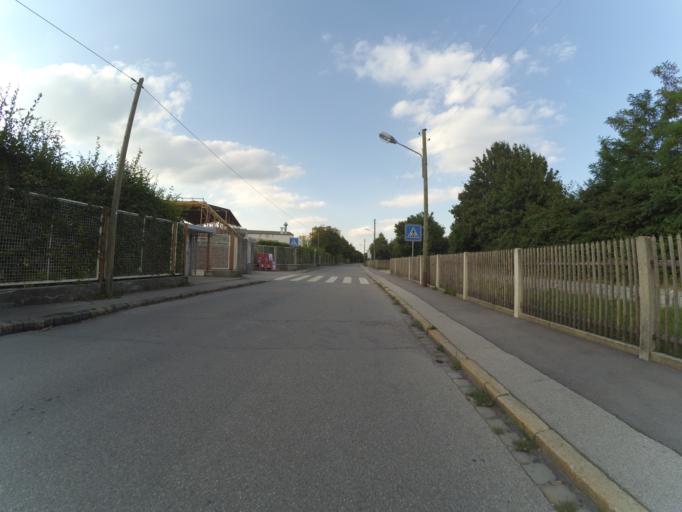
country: DE
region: Bavaria
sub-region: Upper Bavaria
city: Karlsfeld
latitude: 48.1913
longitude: 11.4735
